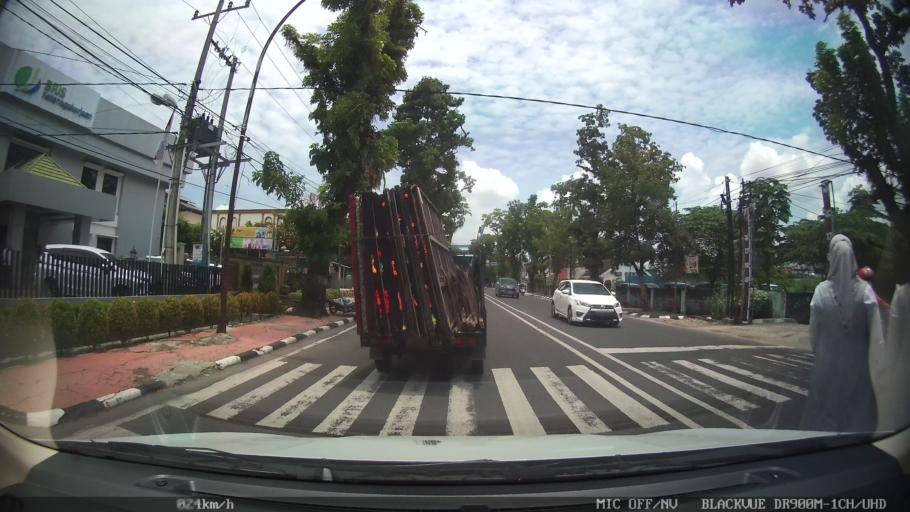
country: ID
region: North Sumatra
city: Medan
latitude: 3.5754
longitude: 98.6658
